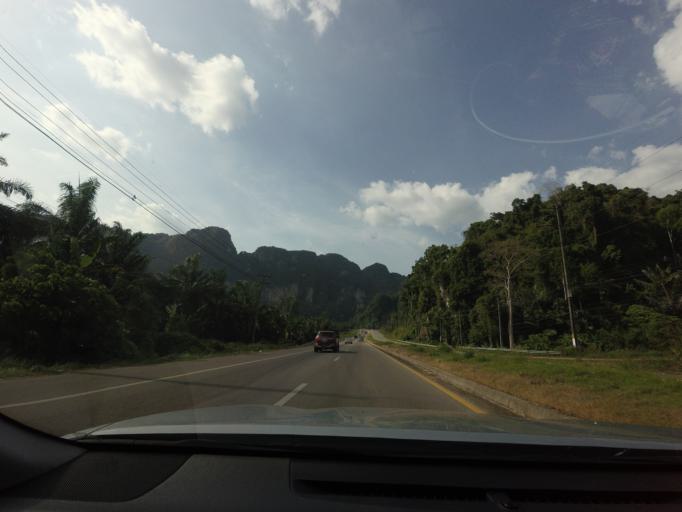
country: TH
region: Krabi
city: Ao Luek
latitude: 8.4092
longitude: 98.7391
